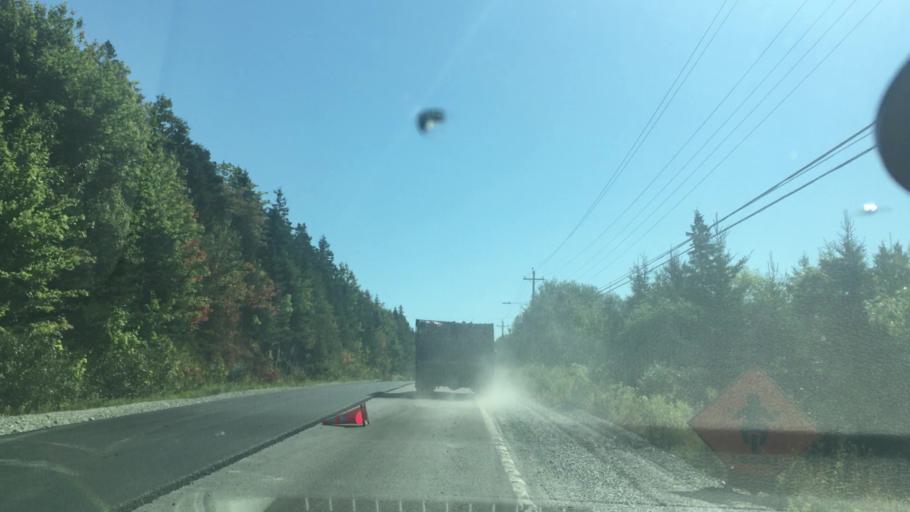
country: CA
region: Nova Scotia
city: New Glasgow
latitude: 44.9102
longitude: -62.5042
